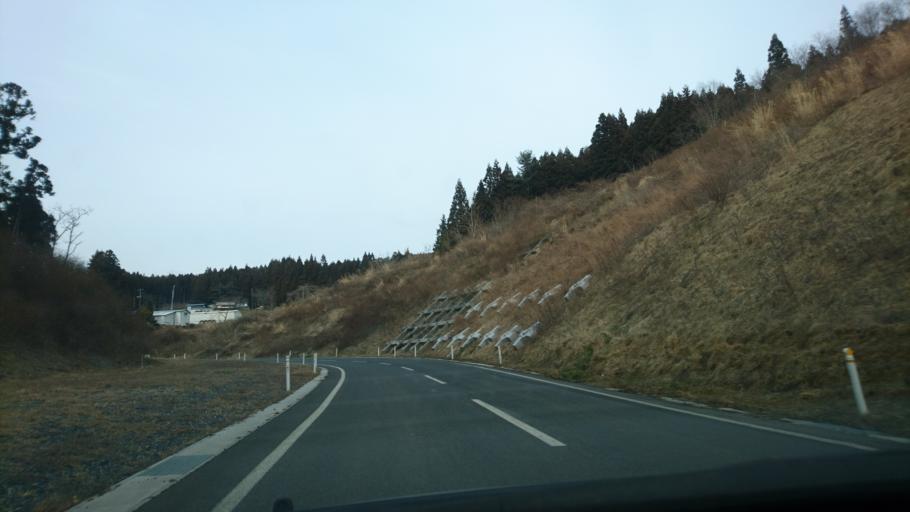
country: JP
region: Iwate
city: Ichinoseki
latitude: 38.8542
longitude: 141.3927
